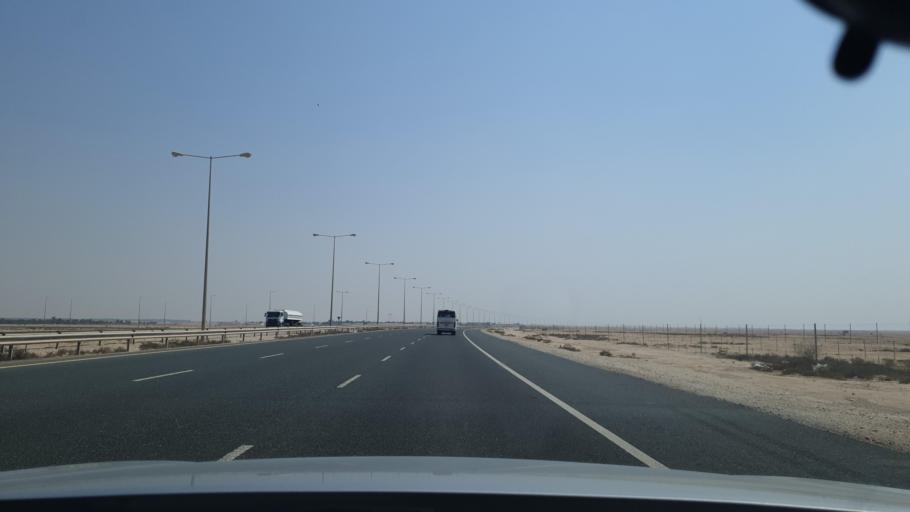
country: QA
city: Al Ghuwayriyah
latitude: 25.8245
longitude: 51.3602
